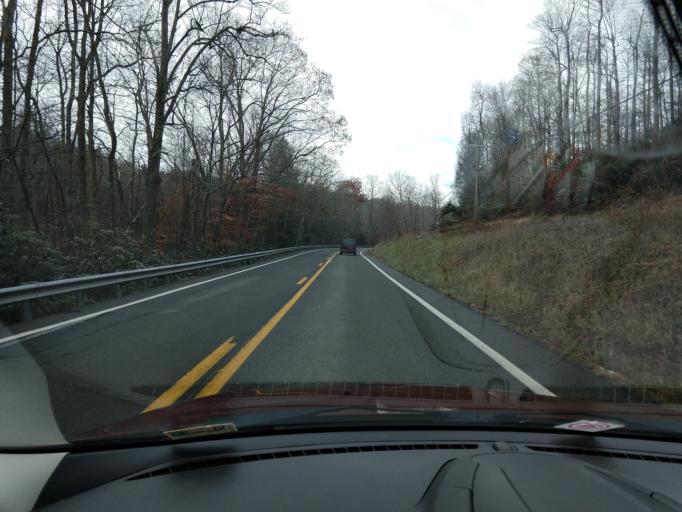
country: US
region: West Virginia
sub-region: Nicholas County
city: Summersville
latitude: 38.2609
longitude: -80.7450
